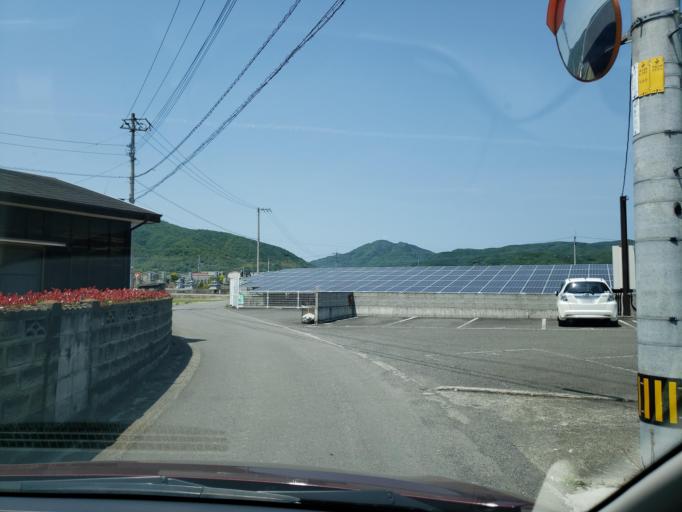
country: JP
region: Tokushima
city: Kamojimacho-jogejima
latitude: 34.0934
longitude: 134.2685
